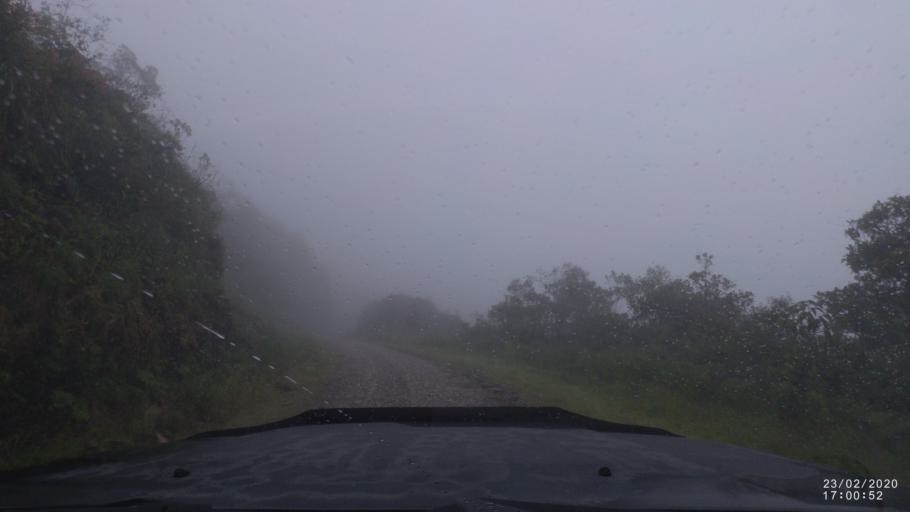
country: BO
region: Cochabamba
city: Colomi
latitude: -17.1128
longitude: -65.9682
